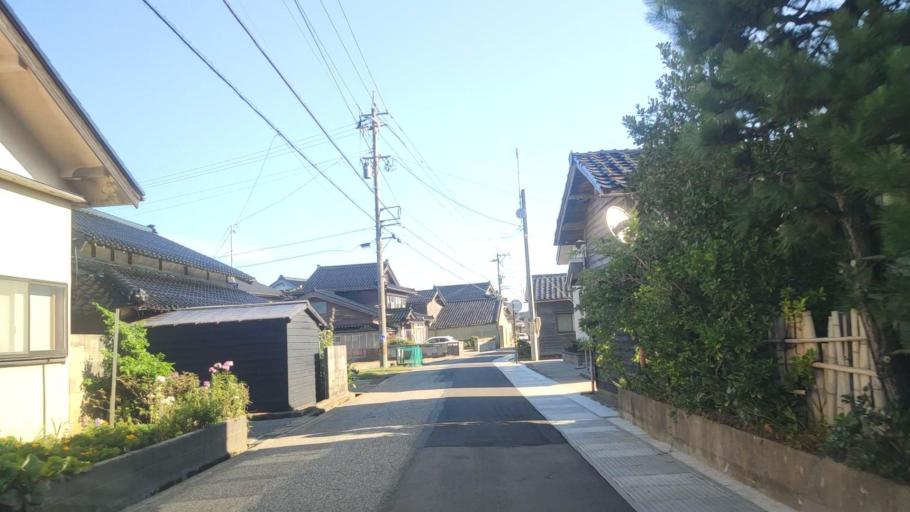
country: JP
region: Ishikawa
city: Hakui
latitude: 36.9505
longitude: 136.7639
